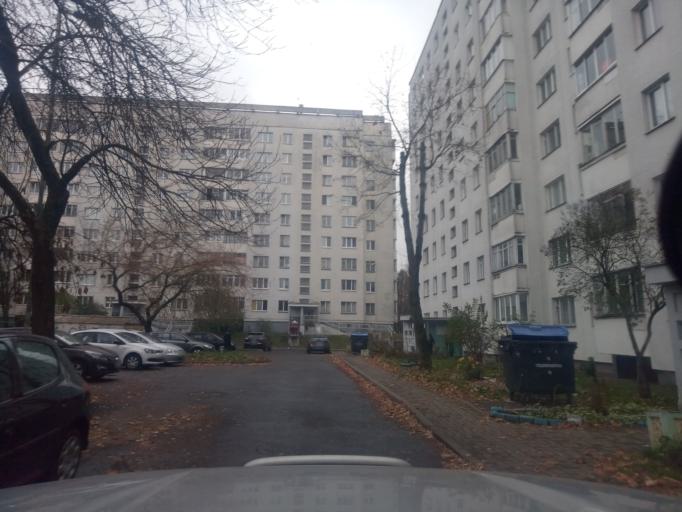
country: BY
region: Minsk
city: Borovlyany
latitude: 53.9345
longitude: 27.6432
